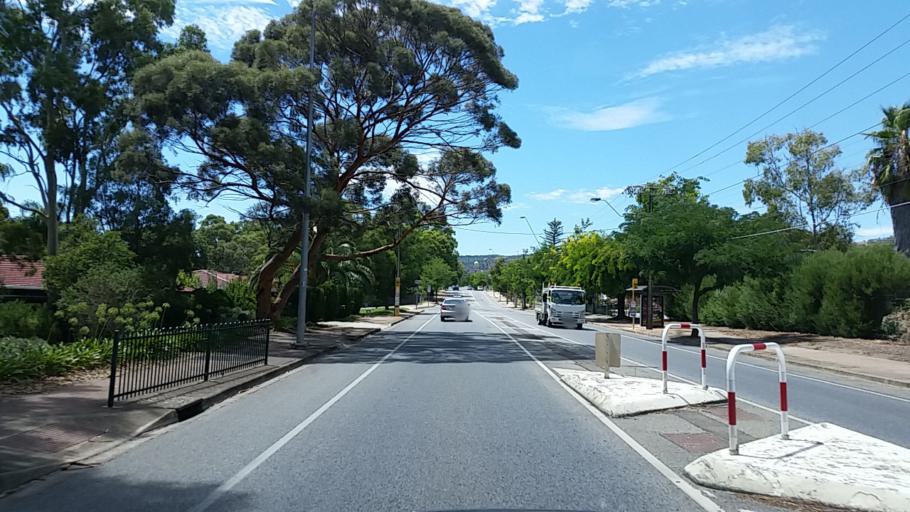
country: AU
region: South Australia
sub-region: Campbelltown
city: Athelstone
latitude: -34.8749
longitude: 138.6961
